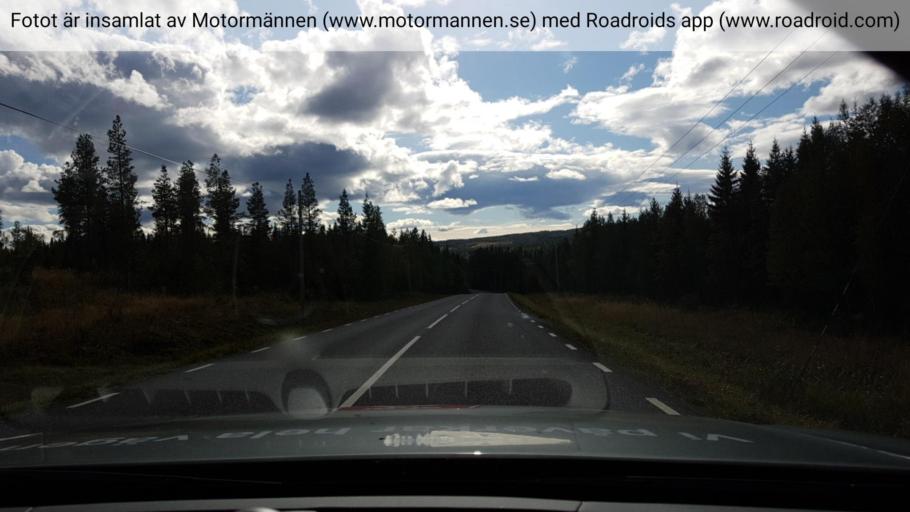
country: SE
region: Jaemtland
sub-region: Are Kommun
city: Jarpen
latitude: 63.4278
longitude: 13.3733
